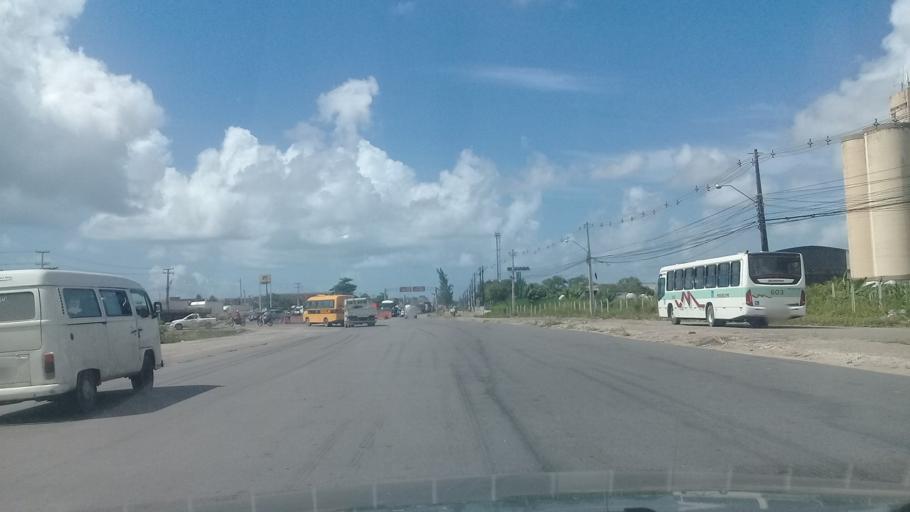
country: BR
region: Pernambuco
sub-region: Jaboatao Dos Guararapes
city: Jaboatao
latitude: -8.1563
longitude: -34.9417
